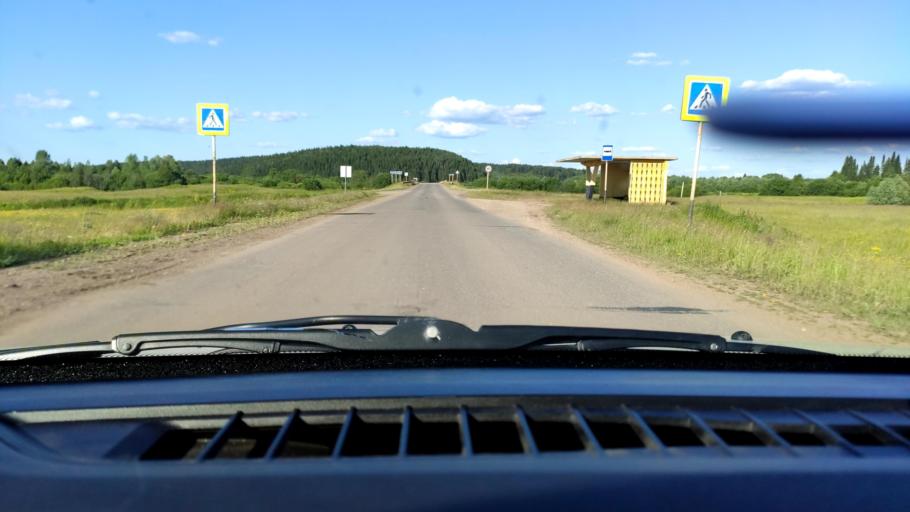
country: RU
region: Perm
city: Uinskoye
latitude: 57.0737
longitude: 56.5941
